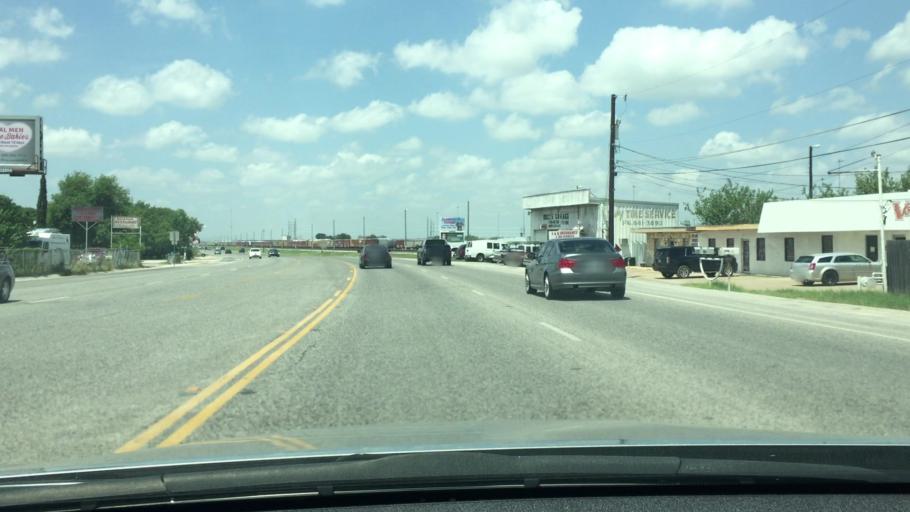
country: US
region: Texas
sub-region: Bexar County
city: Kirby
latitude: 29.4744
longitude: -98.3819
